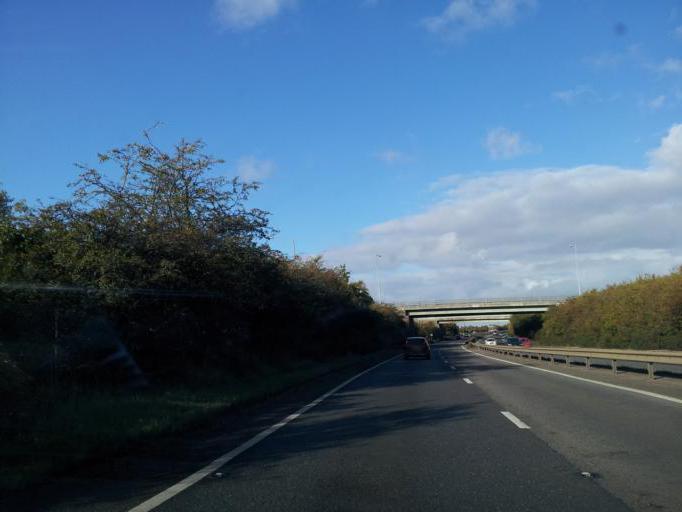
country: GB
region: England
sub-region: Norfolk
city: King's Lynn
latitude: 52.7361
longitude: 0.3968
